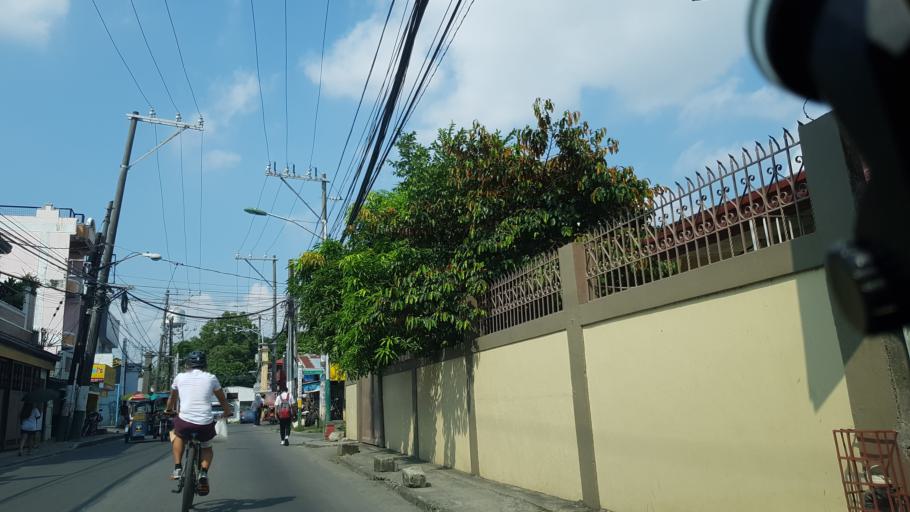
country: PH
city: Sambayanihan People's Village
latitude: 14.4755
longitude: 121.0252
